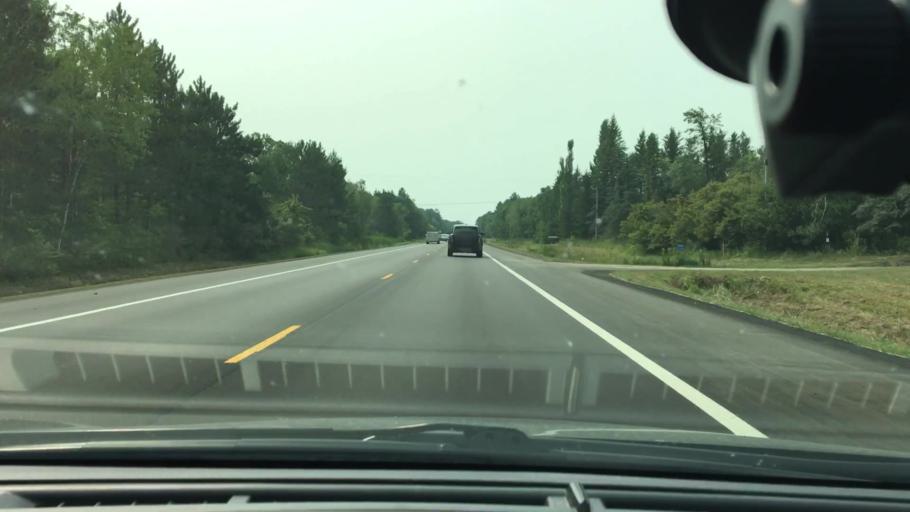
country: US
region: Minnesota
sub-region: Crow Wing County
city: Brainerd
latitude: 46.4472
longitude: -94.1720
